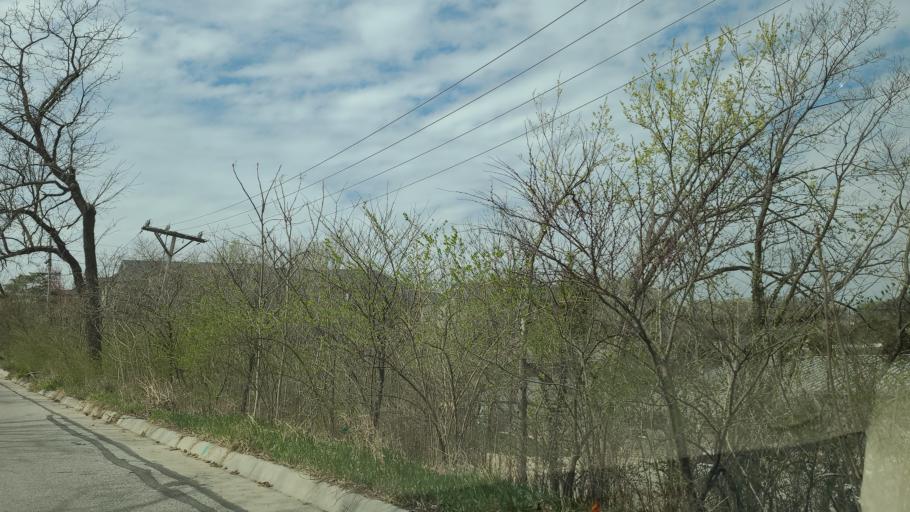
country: US
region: Kansas
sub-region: Douglas County
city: Lawrence
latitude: 38.9715
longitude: -95.2558
